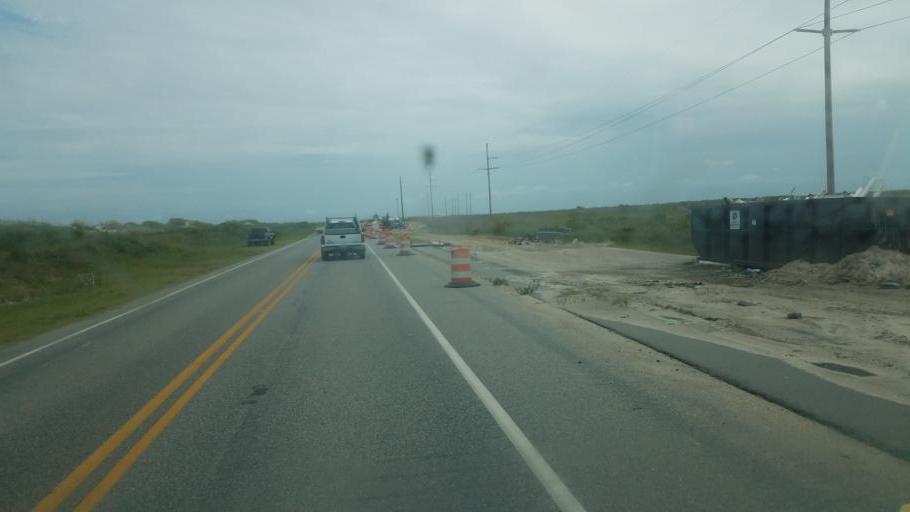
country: US
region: North Carolina
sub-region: Dare County
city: Wanchese
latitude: 35.6912
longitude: -75.4849
